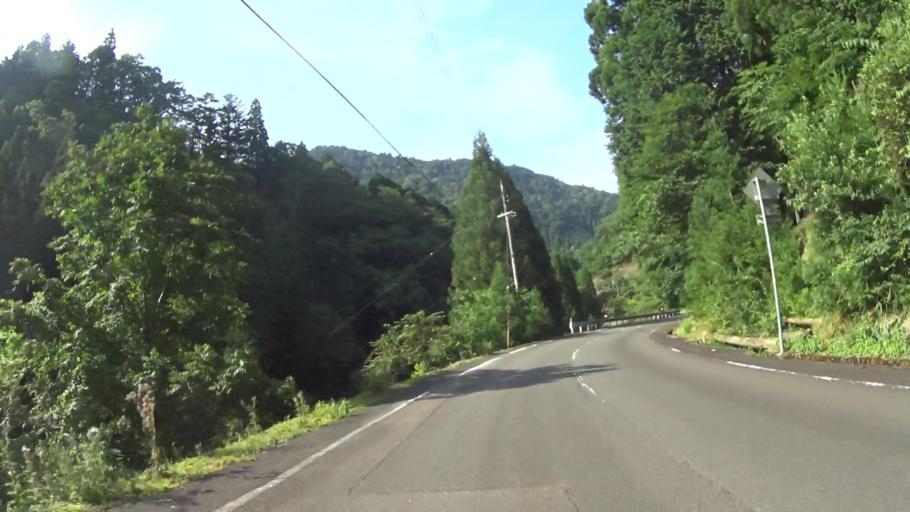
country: JP
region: Fukui
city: Obama
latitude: 35.2759
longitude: 135.6896
